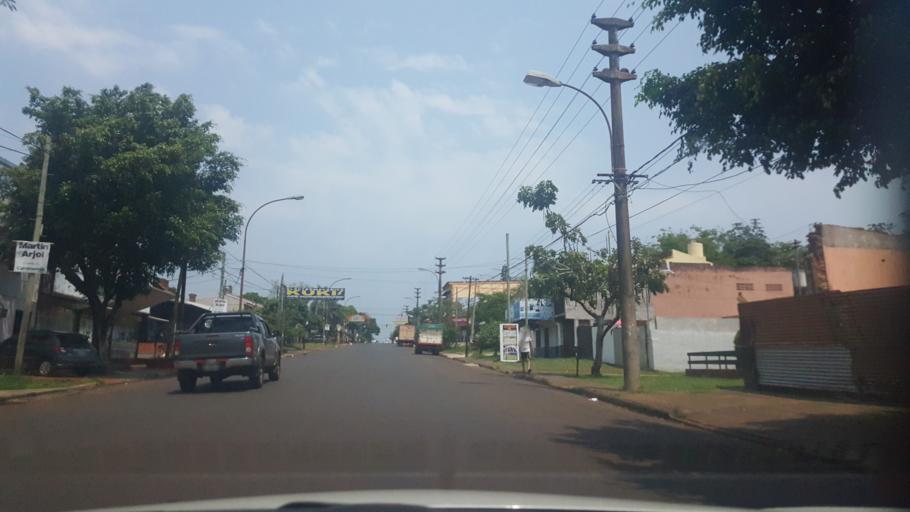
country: AR
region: Misiones
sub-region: Departamento de Capital
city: Posadas
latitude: -27.3886
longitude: -55.9043
